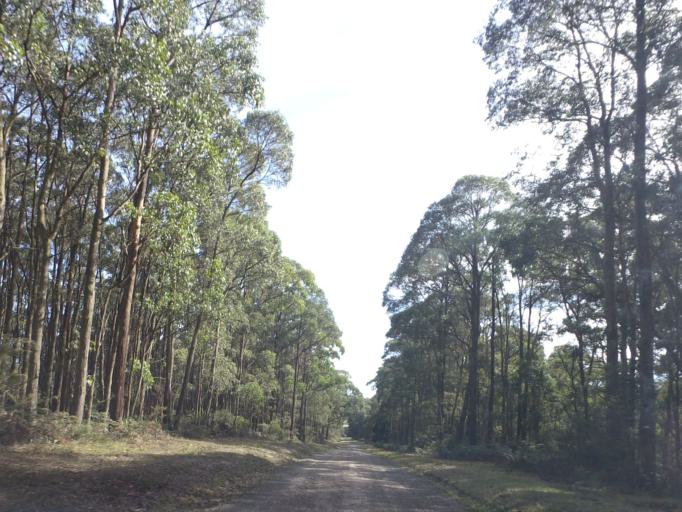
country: AU
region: Victoria
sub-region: Moorabool
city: Bacchus Marsh
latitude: -37.4653
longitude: 144.2156
